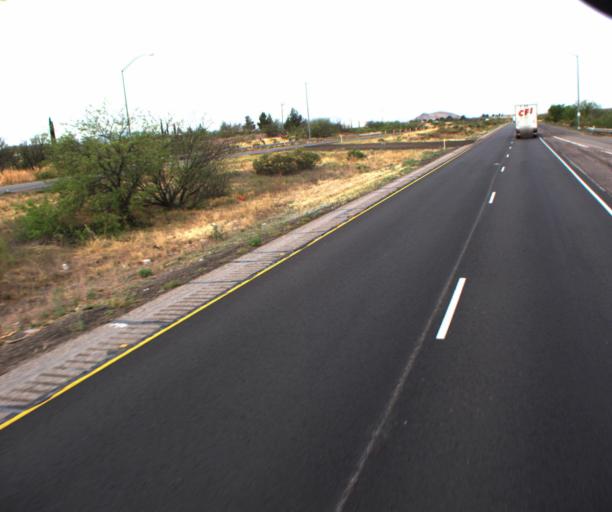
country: US
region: Arizona
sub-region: Cochise County
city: Mescal
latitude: 31.9631
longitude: -110.4375
